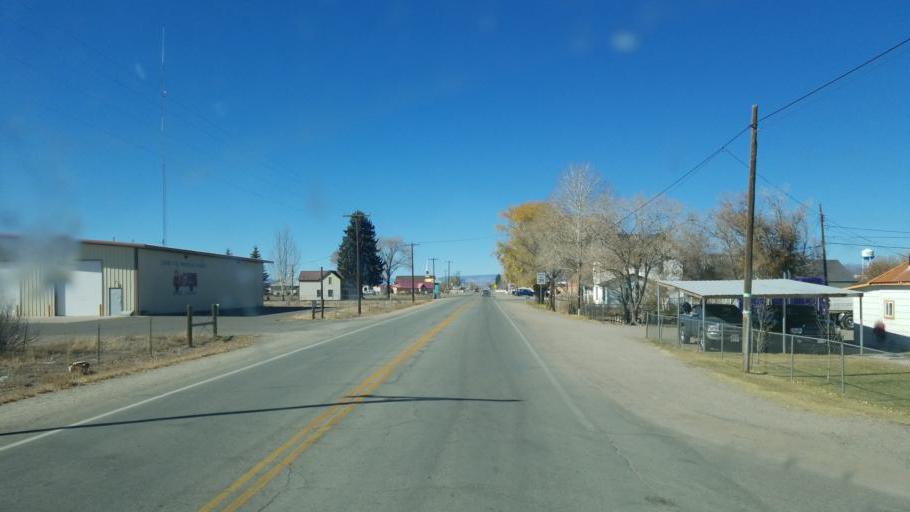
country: US
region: Colorado
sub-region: Saguache County
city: Center
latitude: 37.7483
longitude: -106.1083
